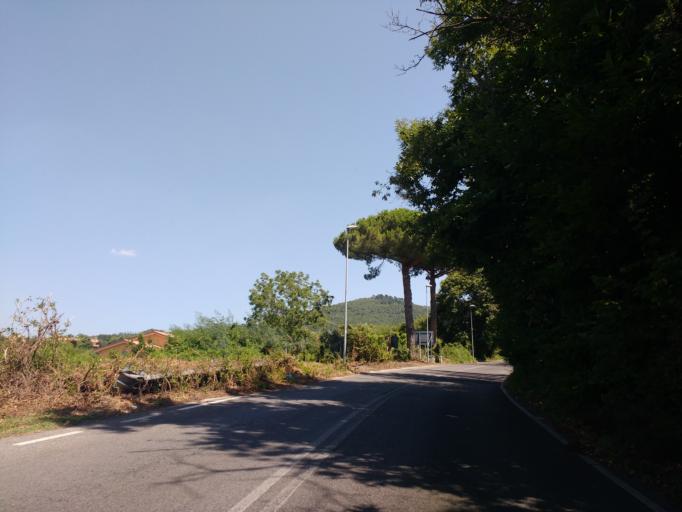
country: IT
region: Latium
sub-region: Citta metropolitana di Roma Capitale
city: Rocca di Papa
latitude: 41.7721
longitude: 12.7012
